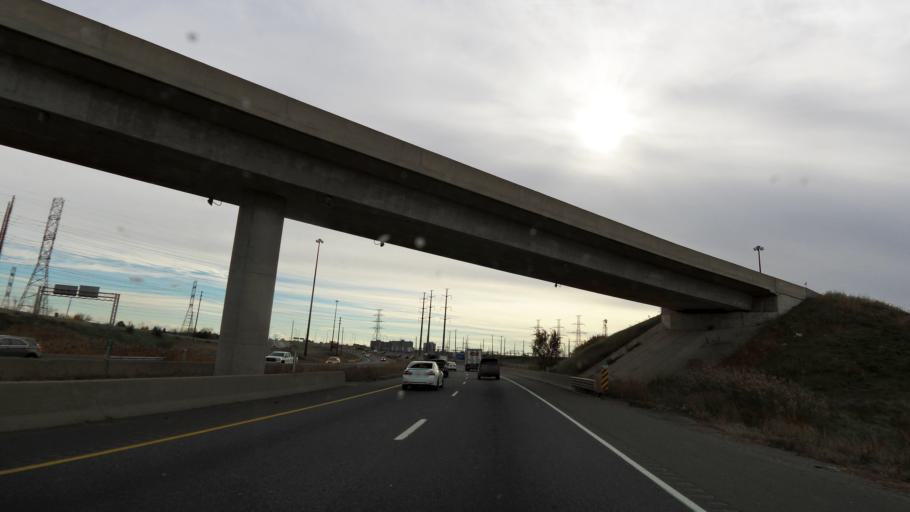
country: CA
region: Ontario
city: Burlington
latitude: 43.3365
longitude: -79.8295
